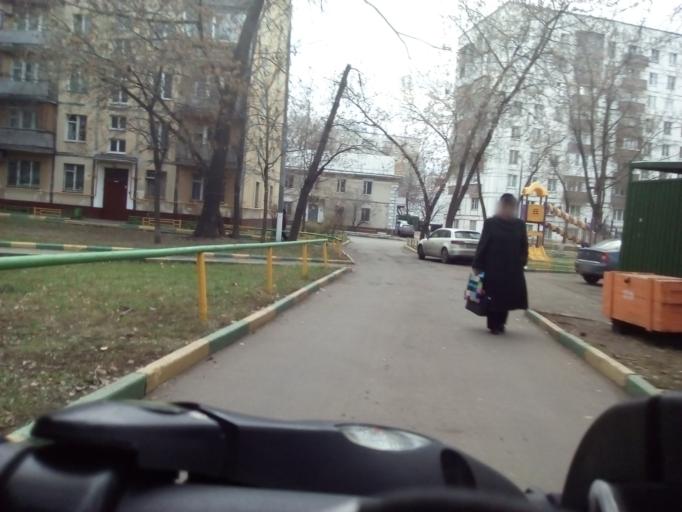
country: RU
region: Moscow
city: Lefortovo
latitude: 55.7731
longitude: 37.7117
